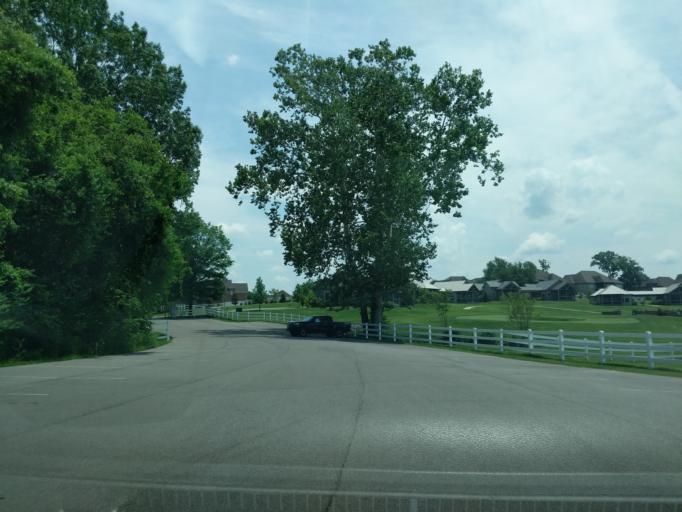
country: US
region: Tennessee
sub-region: Davidson County
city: Lakewood
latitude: 36.2340
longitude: -86.6365
